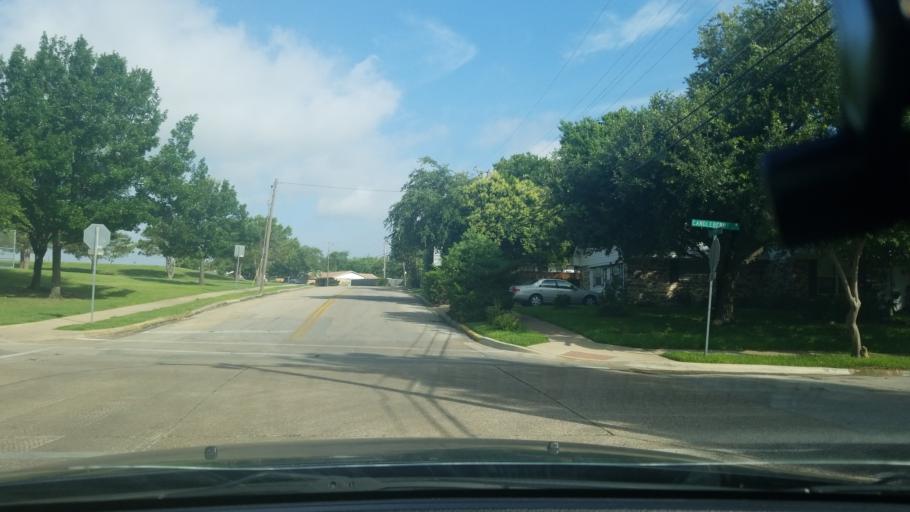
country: US
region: Texas
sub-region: Dallas County
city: Mesquite
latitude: 32.7707
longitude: -96.6320
